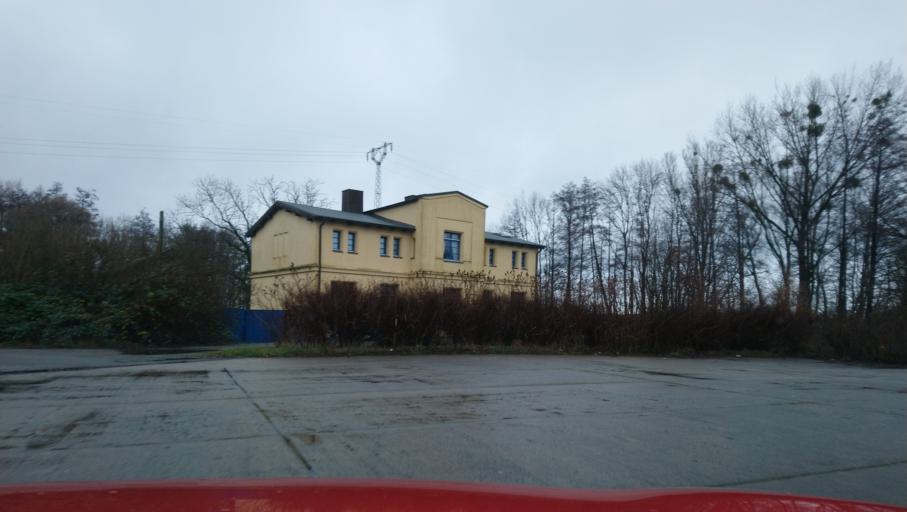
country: DE
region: Mecklenburg-Vorpommern
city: Seehof
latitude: 53.6786
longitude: 11.4499
